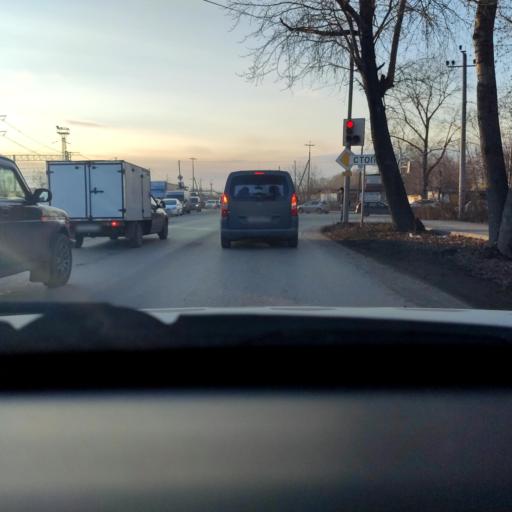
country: RU
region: Perm
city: Froly
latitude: 57.9537
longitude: 56.2420
